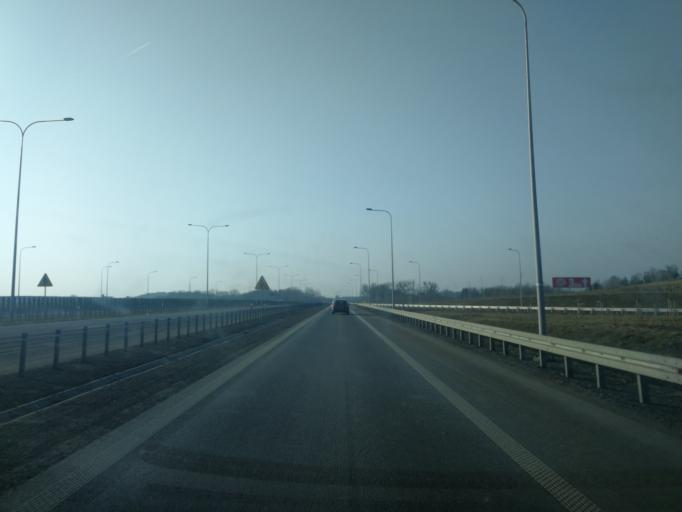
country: PL
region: Warmian-Masurian Voivodeship
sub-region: Powiat ostrodzki
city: Ostroda
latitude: 53.6857
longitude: 20.0052
